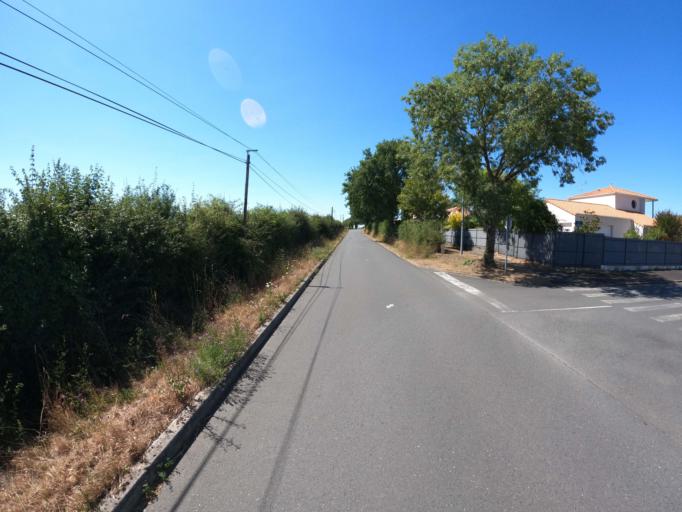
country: FR
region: Pays de la Loire
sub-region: Departement de Maine-et-Loire
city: Saint-Christophe-du-Bois
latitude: 47.0286
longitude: -0.9513
